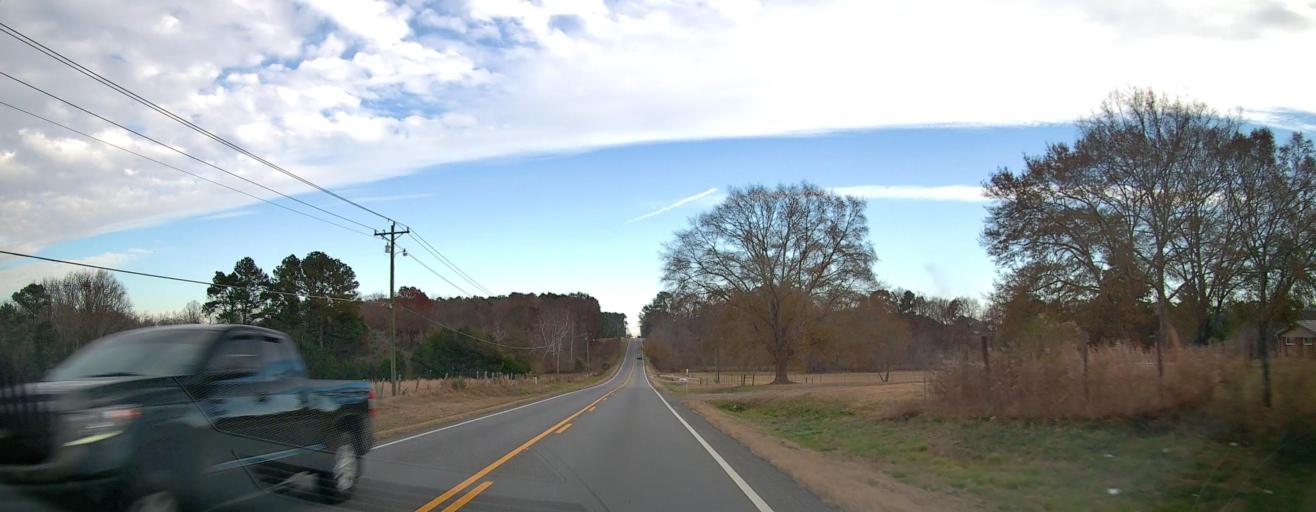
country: US
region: Alabama
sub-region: Morgan County
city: Priceville
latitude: 34.4544
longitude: -86.7694
